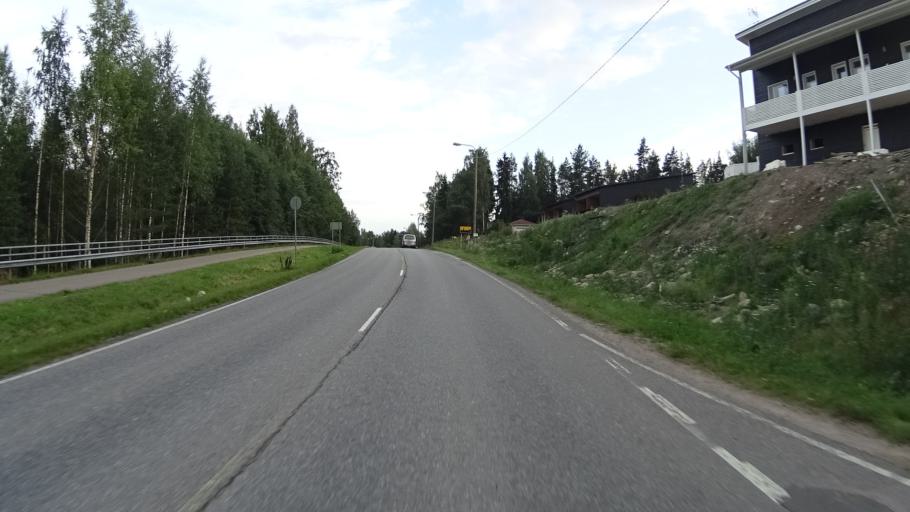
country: FI
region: Uusimaa
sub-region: Helsinki
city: Kilo
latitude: 60.3329
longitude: 24.8626
